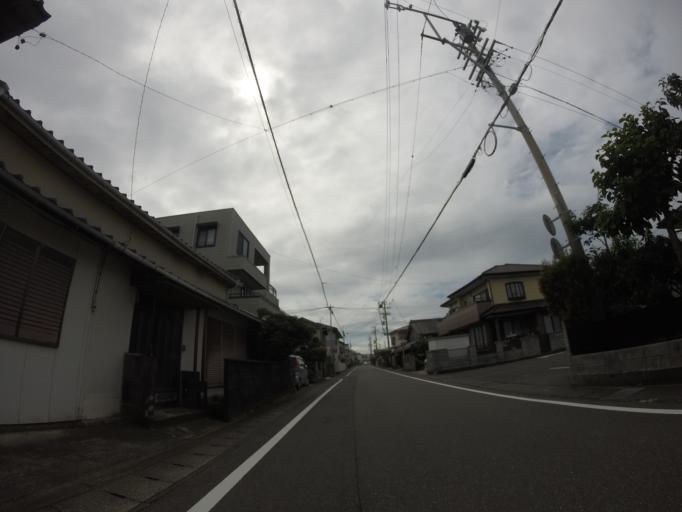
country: JP
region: Shizuoka
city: Oyama
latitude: 34.6027
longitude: 138.2188
